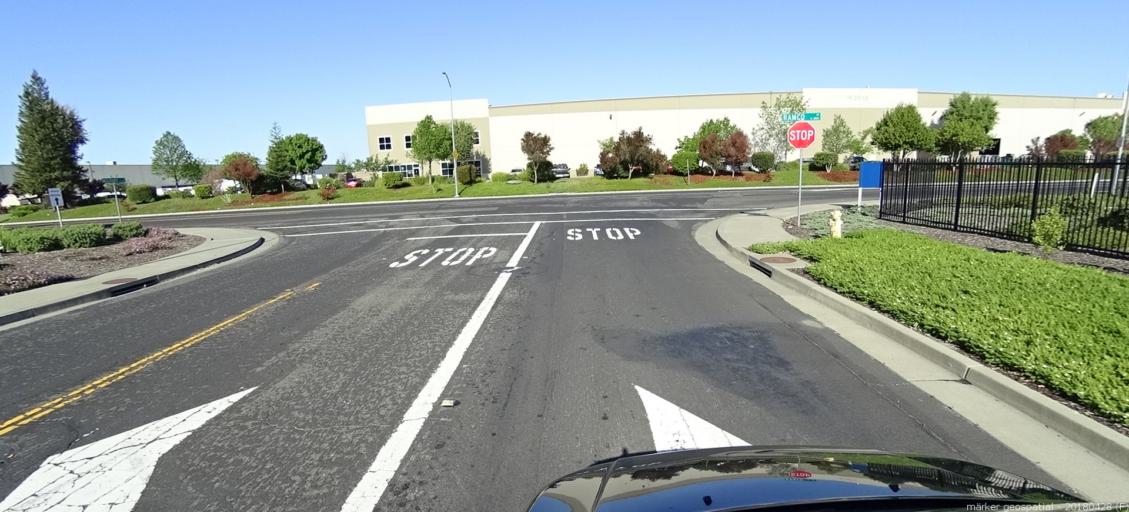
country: US
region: California
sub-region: Yolo County
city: West Sacramento
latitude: 38.5493
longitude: -121.5626
